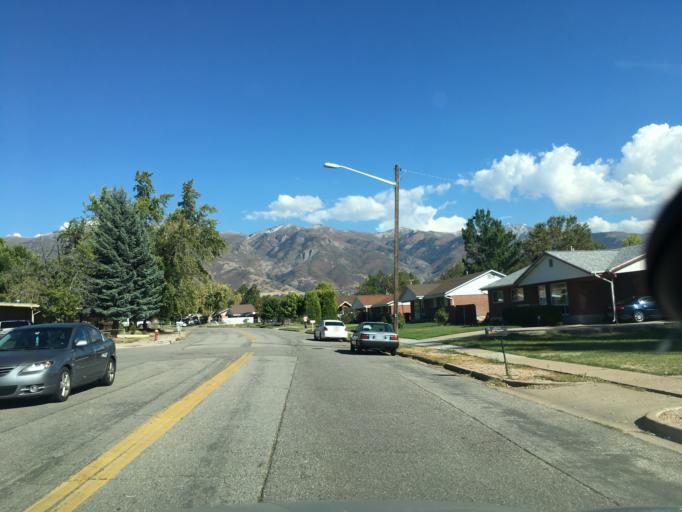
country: US
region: Utah
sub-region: Davis County
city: Layton
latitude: 41.0662
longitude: -111.9568
